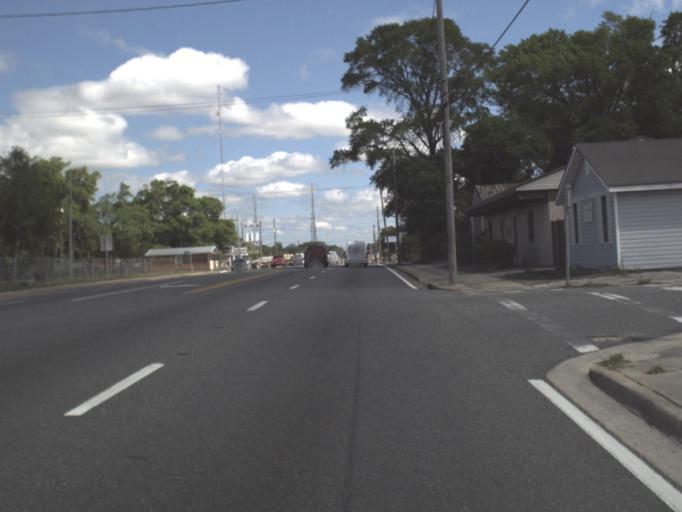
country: US
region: Florida
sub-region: Escambia County
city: Pensacola
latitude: 30.4251
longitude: -87.2409
